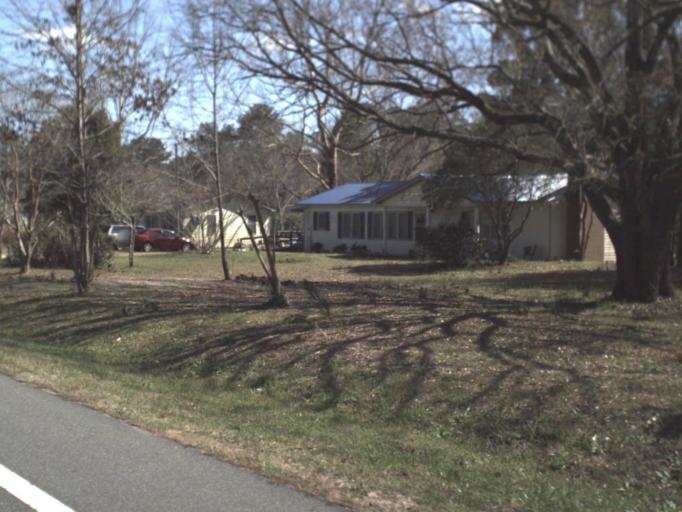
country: US
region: Florida
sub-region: Gadsden County
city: Chattahoochee
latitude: 30.7023
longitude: -84.7856
